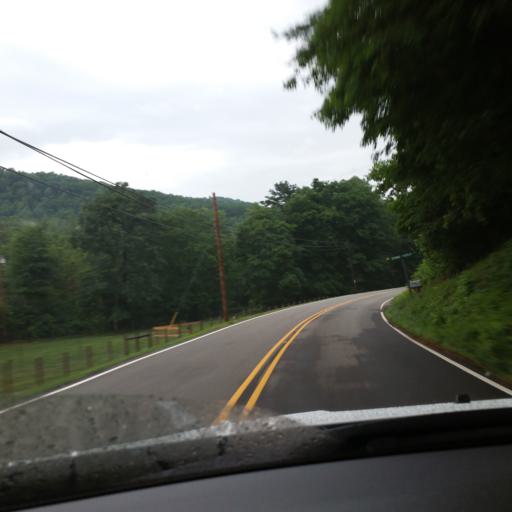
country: US
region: North Carolina
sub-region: Yancey County
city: Burnsville
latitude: 35.8165
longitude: -82.1925
